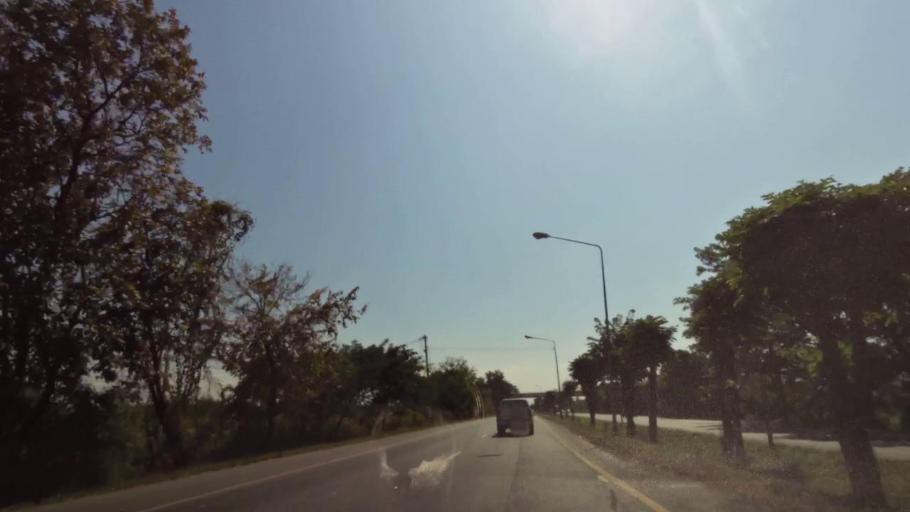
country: TH
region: Nakhon Sawan
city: Kao Liao
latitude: 15.7960
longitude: 100.1206
